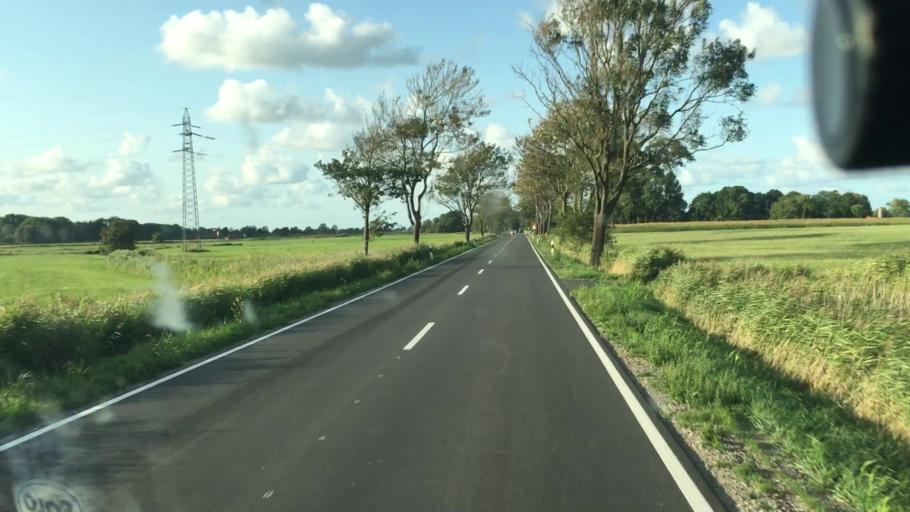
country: DE
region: Lower Saxony
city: Jever
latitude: 53.6348
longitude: 7.8613
